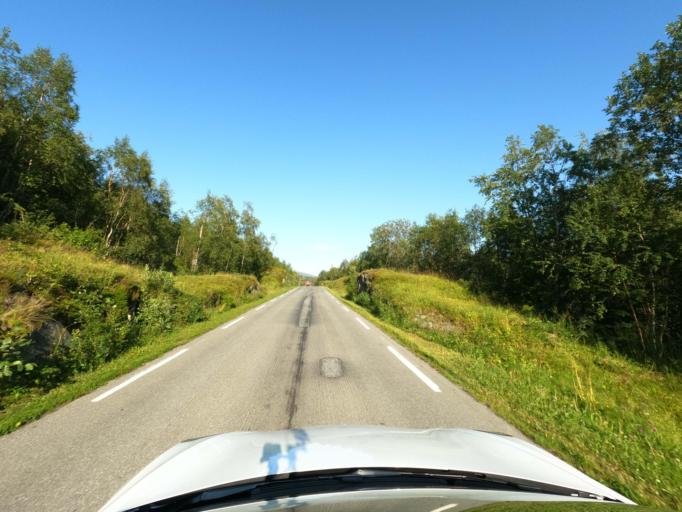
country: NO
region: Nordland
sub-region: Narvik
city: Bjerkvik
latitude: 68.5527
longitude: 17.5805
